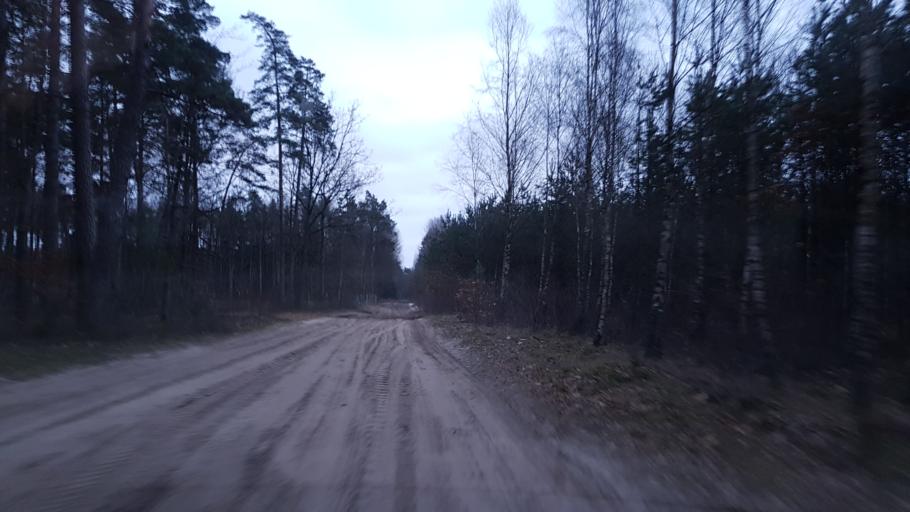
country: PL
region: Greater Poland Voivodeship
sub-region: Powiat zlotowski
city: Sypniewo
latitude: 53.4923
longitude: 16.6850
